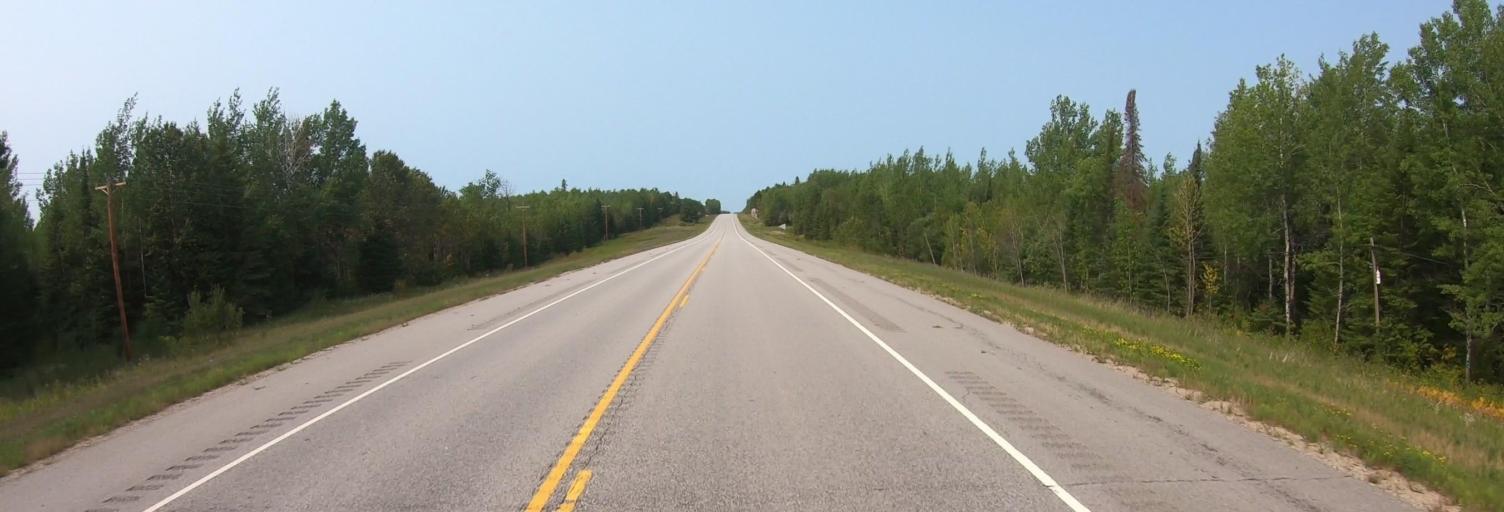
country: CA
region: Ontario
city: Fort Frances
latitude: 48.4087
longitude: -93.0765
